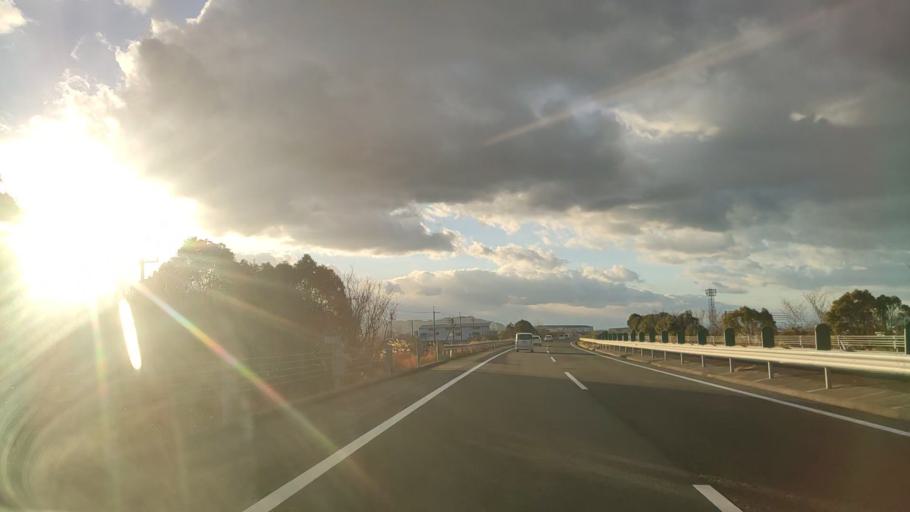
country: JP
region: Ehime
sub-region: Shikoku-chuo Shi
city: Matsuyama
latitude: 33.7848
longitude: 132.8496
